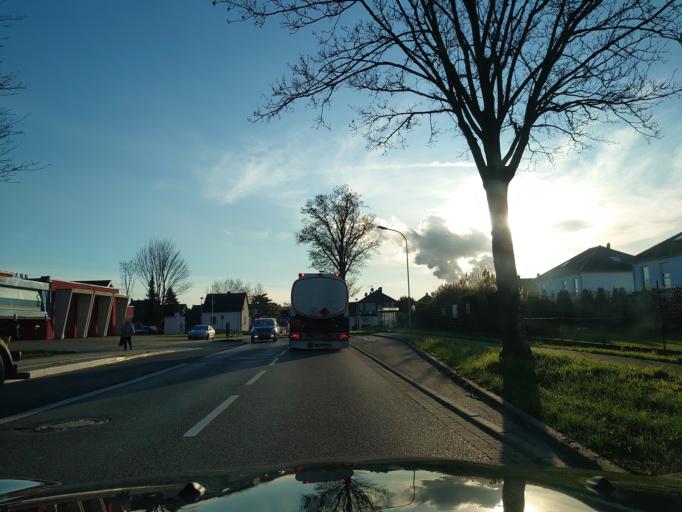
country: DE
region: North Rhine-Westphalia
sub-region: Regierungsbezirk Dusseldorf
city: Rommerskirchen
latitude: 51.0505
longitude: 6.7134
